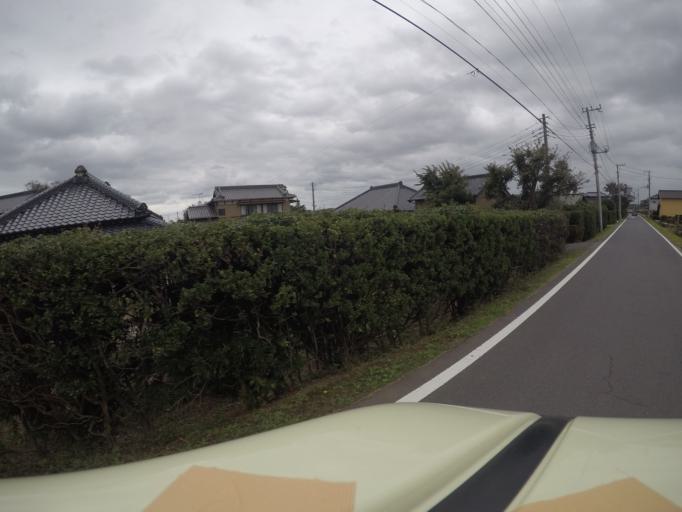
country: JP
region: Ibaraki
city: Inashiki
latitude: 36.0938
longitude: 140.4062
